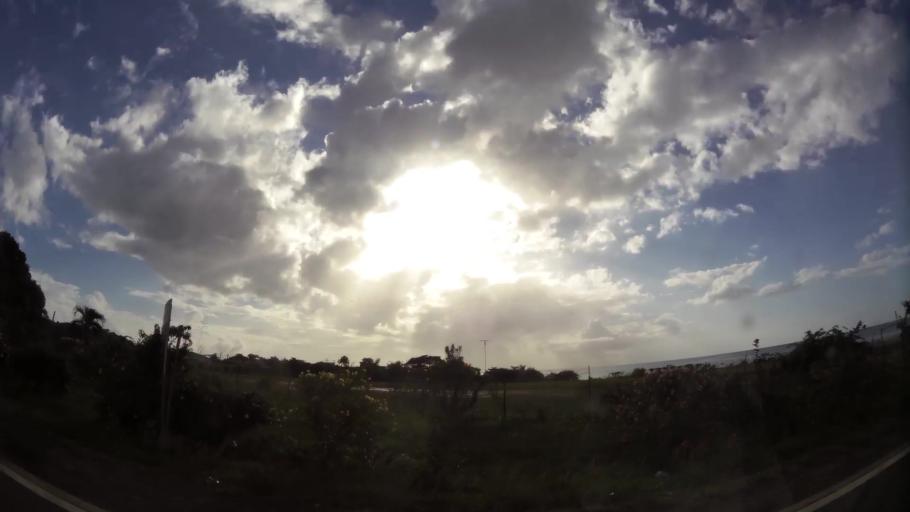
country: DM
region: Saint Paul
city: Mahaut
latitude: 15.3361
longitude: -61.3916
